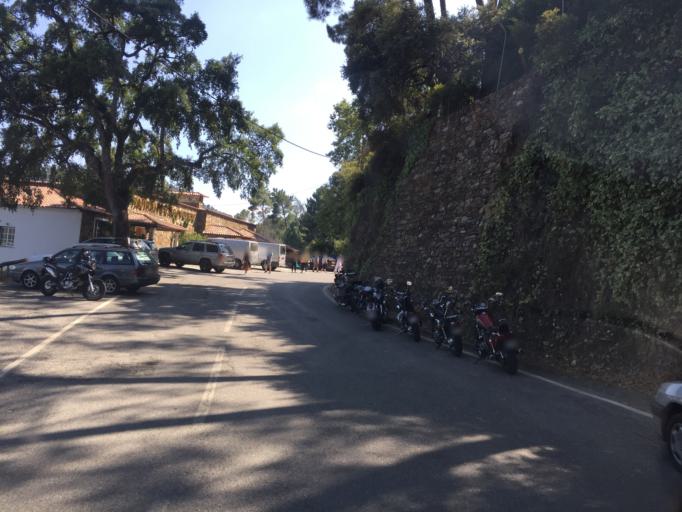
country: PT
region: Leiria
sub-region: Pedrogao Grande
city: Pedrogao Grande
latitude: 39.9234
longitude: -8.1331
